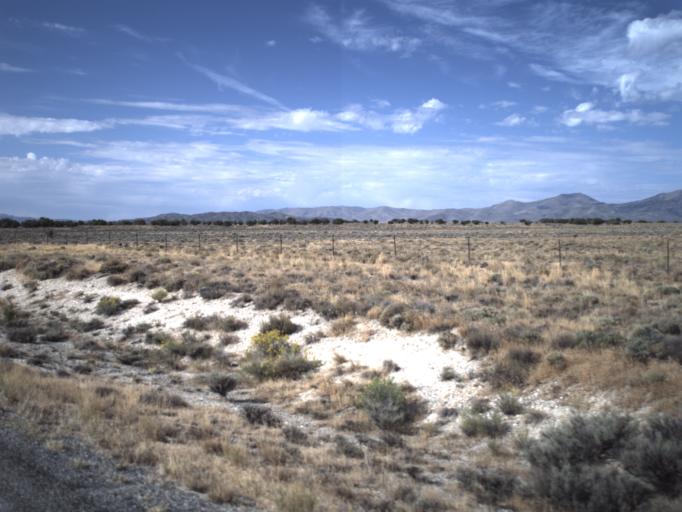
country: US
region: Idaho
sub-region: Cassia County
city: Burley
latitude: 41.7243
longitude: -113.5253
